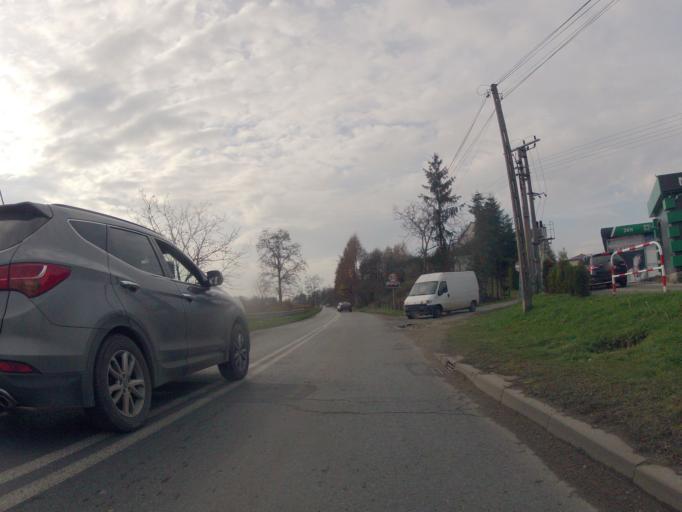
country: PL
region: Lesser Poland Voivodeship
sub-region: Powiat krakowski
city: Rzaska
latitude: 50.0915
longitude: 19.8244
